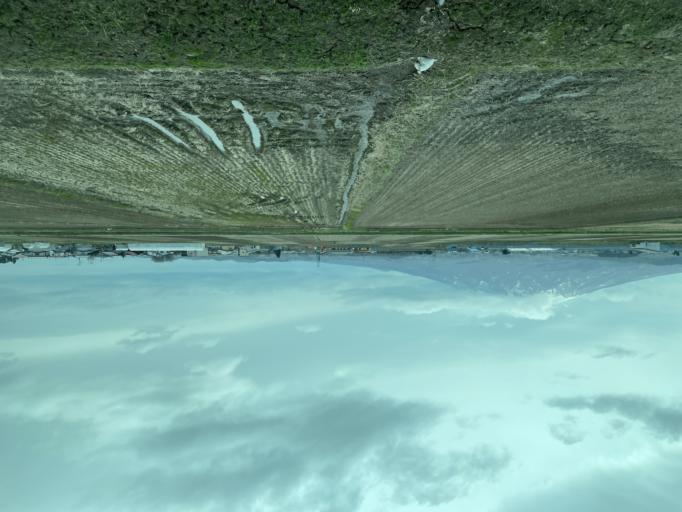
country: JP
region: Aomori
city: Goshogawara
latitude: 40.7343
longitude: 140.4381
